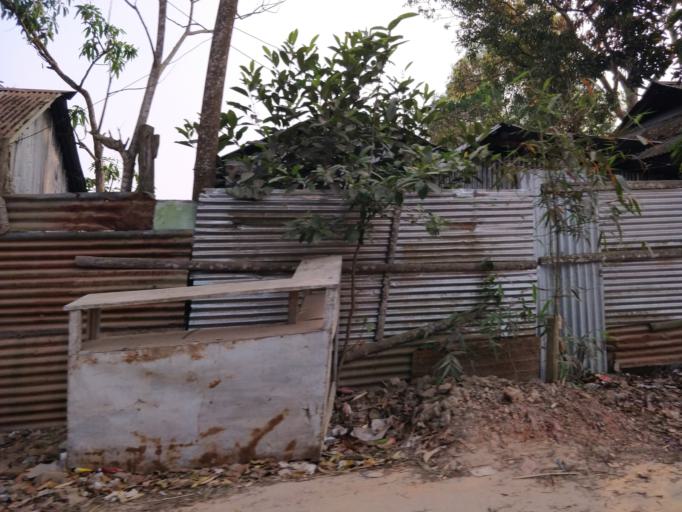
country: IN
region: Tripura
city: Khowai
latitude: 24.1302
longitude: 91.3674
